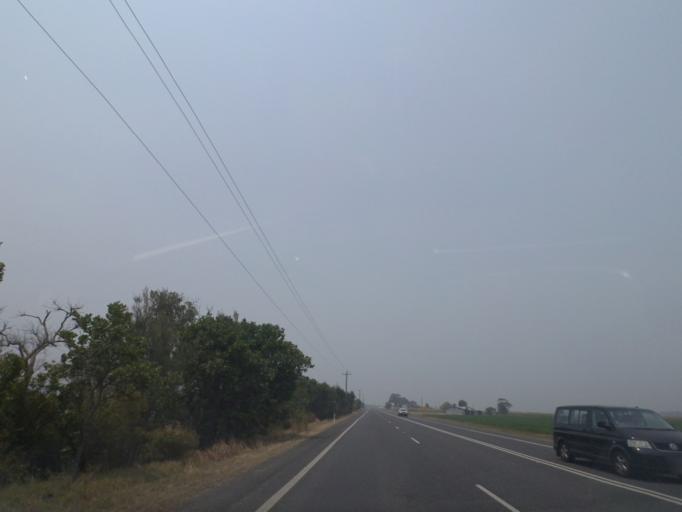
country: AU
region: New South Wales
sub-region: Richmond Valley
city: Evans Head
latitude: -28.9976
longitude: 153.4499
